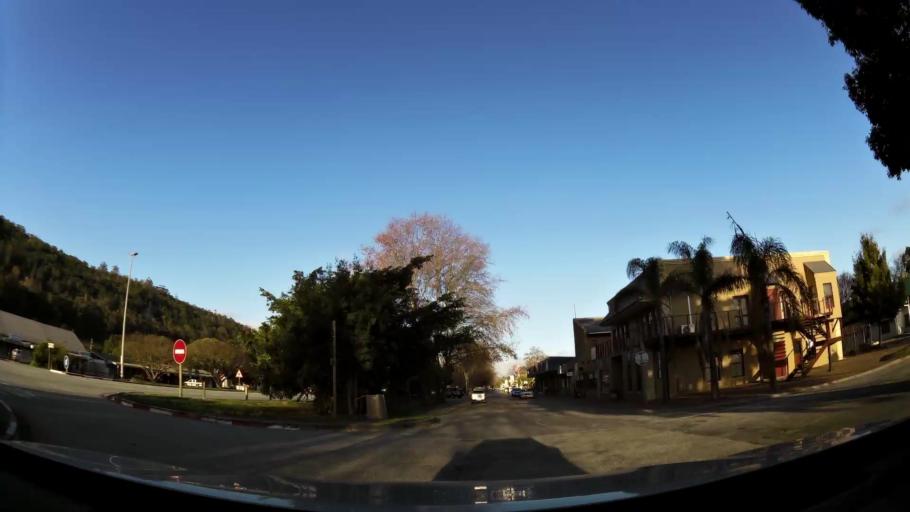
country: ZA
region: Western Cape
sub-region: Eden District Municipality
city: Knysna
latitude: -34.0135
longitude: 22.8000
